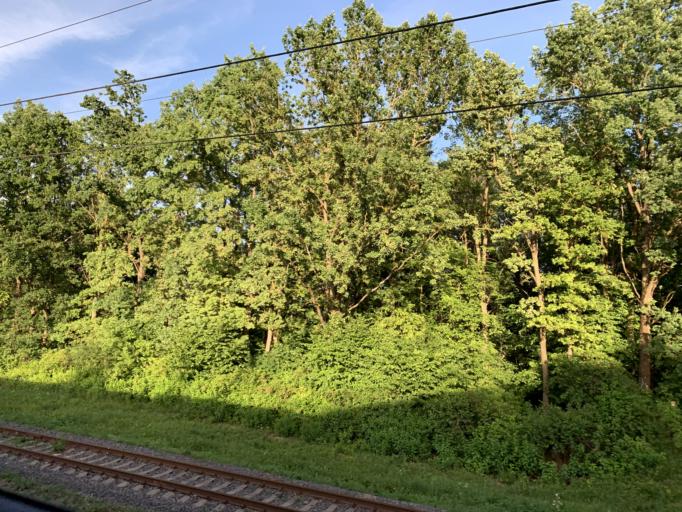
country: BY
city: Fanipol
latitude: 53.7561
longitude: 27.3598
